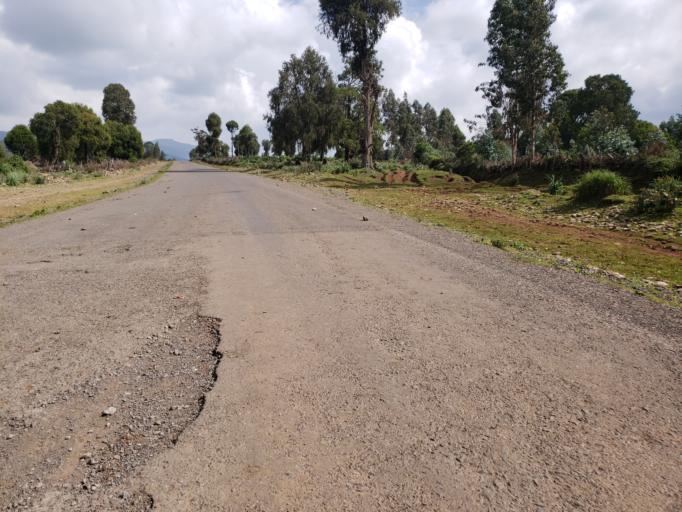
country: ET
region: Oromiya
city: Dodola
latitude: 6.8640
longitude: 39.3915
